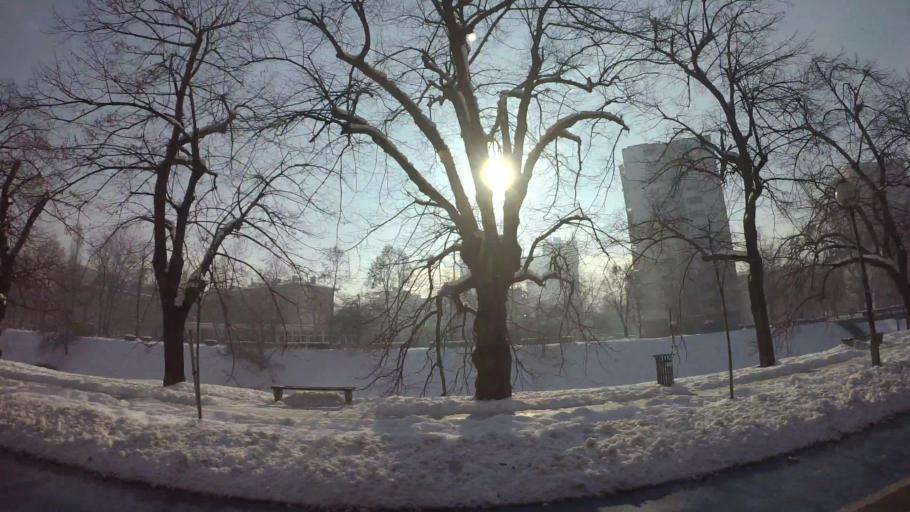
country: BA
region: Federation of Bosnia and Herzegovina
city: Kobilja Glava
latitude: 43.8524
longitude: 18.3905
